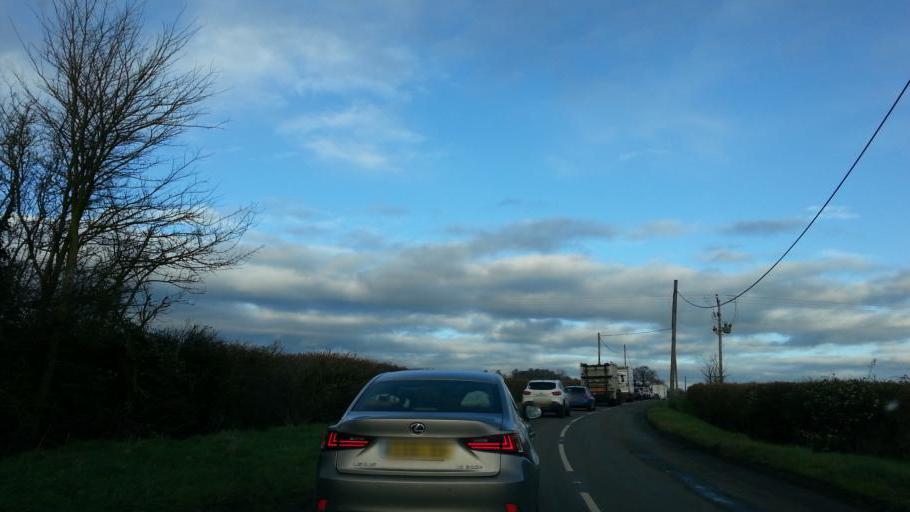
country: GB
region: England
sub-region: Oxfordshire
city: Faringdon
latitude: 51.6195
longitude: -1.5918
